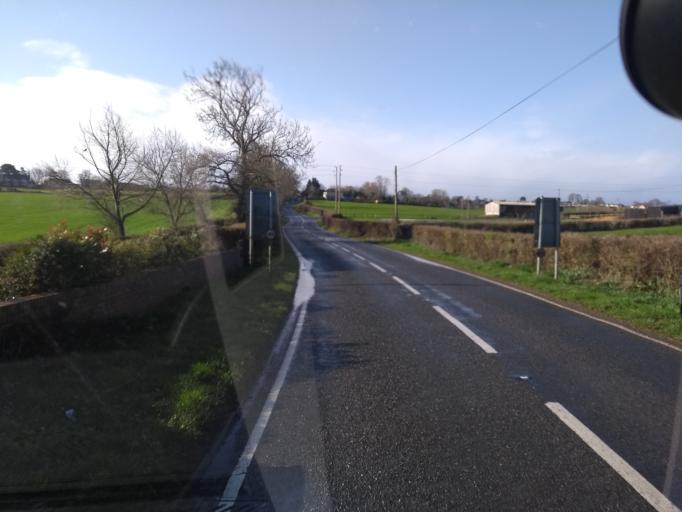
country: GB
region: England
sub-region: Somerset
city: Yeovil
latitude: 50.9645
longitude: -2.6185
